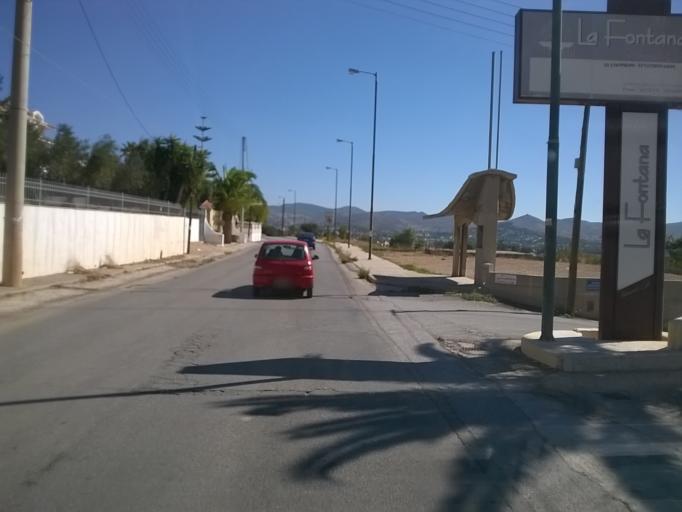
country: GR
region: Attica
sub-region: Nomarchia Anatolikis Attikis
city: Anavyssos
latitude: 37.7359
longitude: 23.9357
